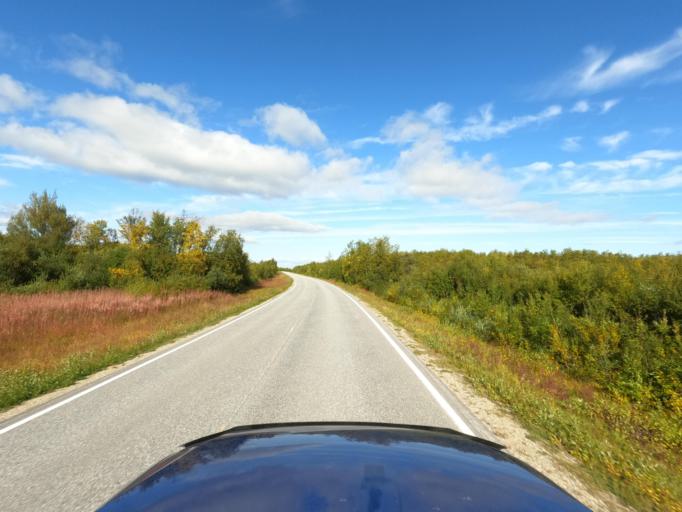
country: NO
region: Finnmark Fylke
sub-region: Karasjok
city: Karasjohka
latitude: 69.5990
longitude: 25.3294
